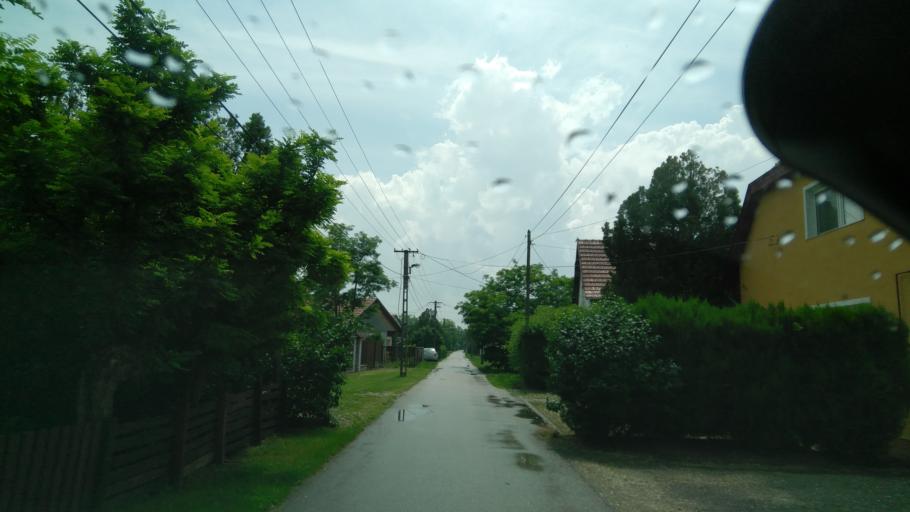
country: HU
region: Bekes
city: Bekescsaba
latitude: 46.6625
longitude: 21.1716
